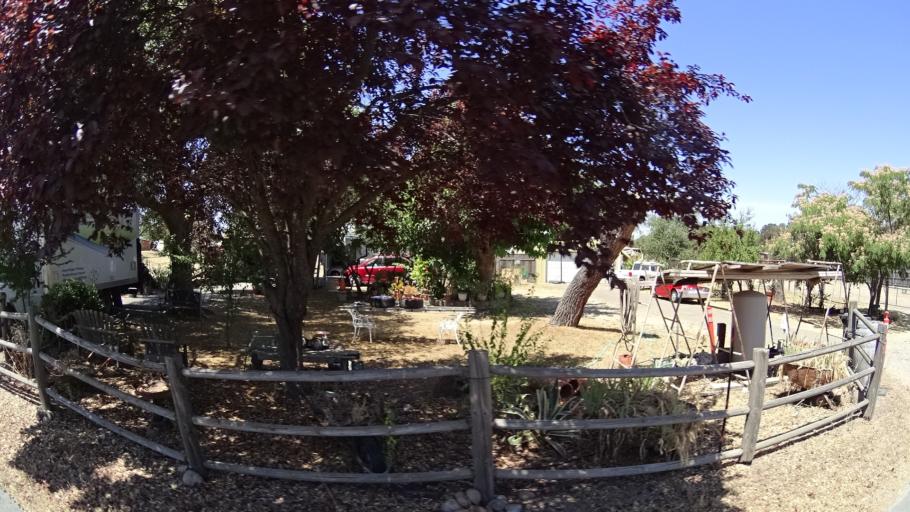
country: US
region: California
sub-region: Calaveras County
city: Rancho Calaveras
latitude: 38.1376
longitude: -120.9133
